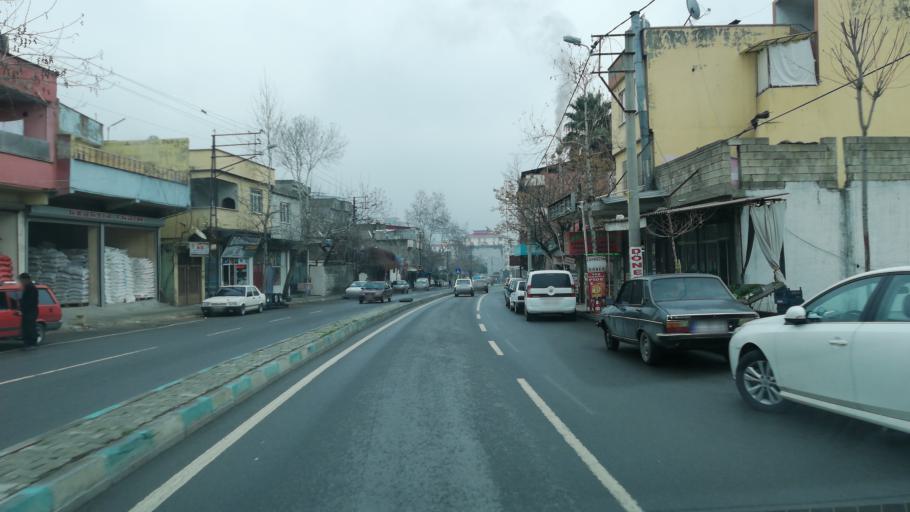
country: TR
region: Kahramanmaras
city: Kahramanmaras
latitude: 37.5823
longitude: 36.9478
